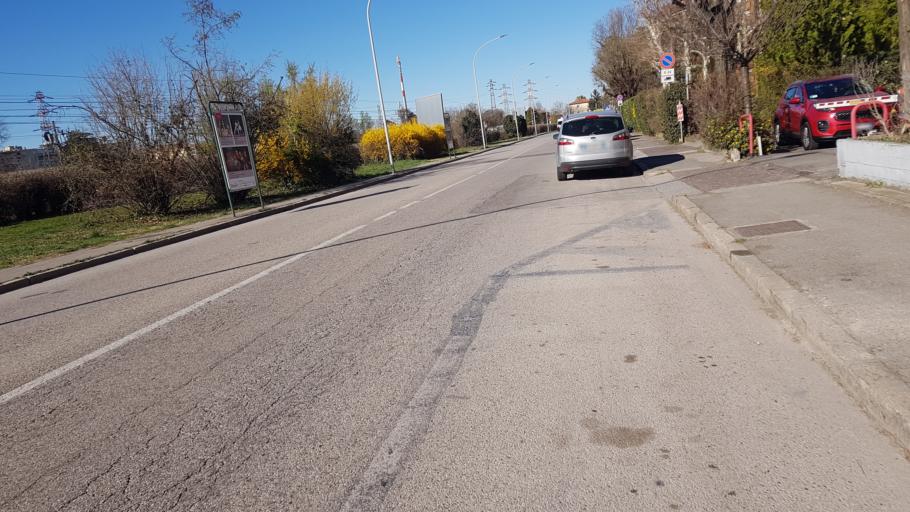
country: IT
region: Emilia-Romagna
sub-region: Provincia di Bologna
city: Bologna
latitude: 44.5194
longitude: 11.3245
